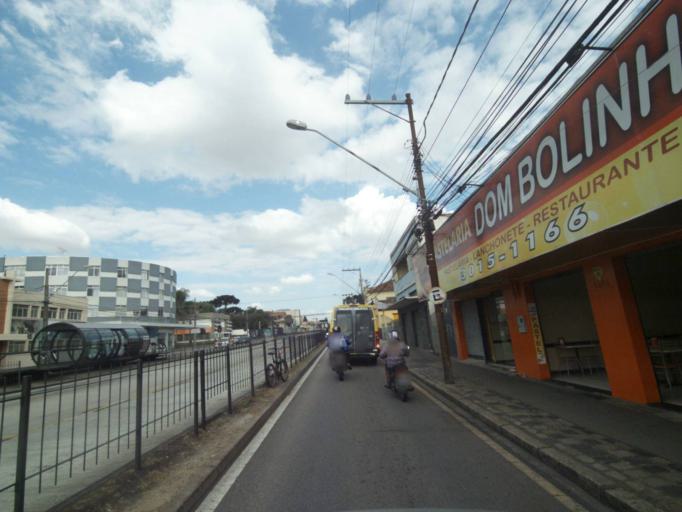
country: BR
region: Parana
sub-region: Curitiba
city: Curitiba
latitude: -25.4473
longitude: -49.2640
